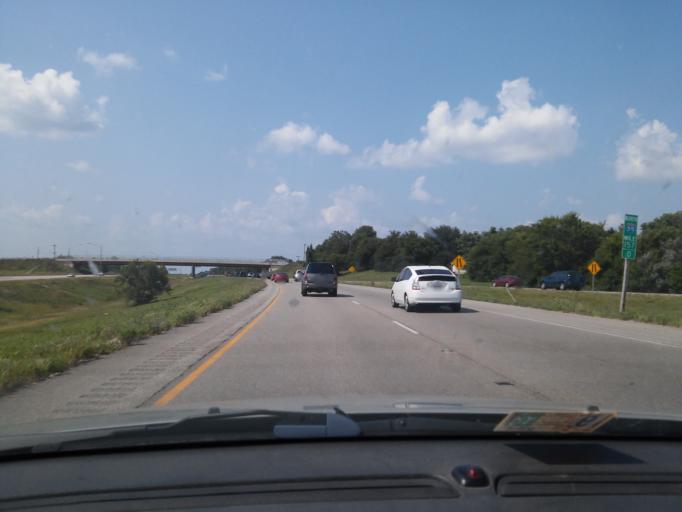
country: US
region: Illinois
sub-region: McLean County
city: Bloomington
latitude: 40.4467
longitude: -89.0212
